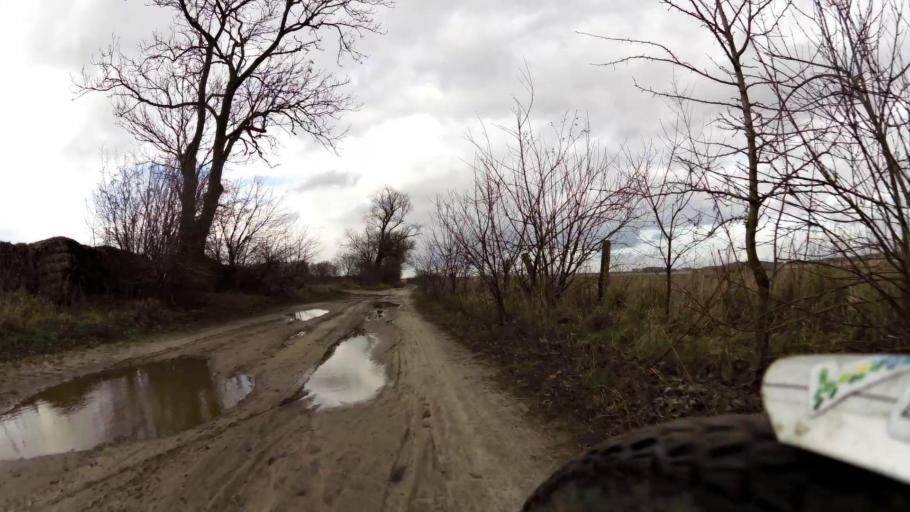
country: PL
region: West Pomeranian Voivodeship
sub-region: Powiat kamienski
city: Kamien Pomorski
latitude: 53.8816
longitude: 14.7148
